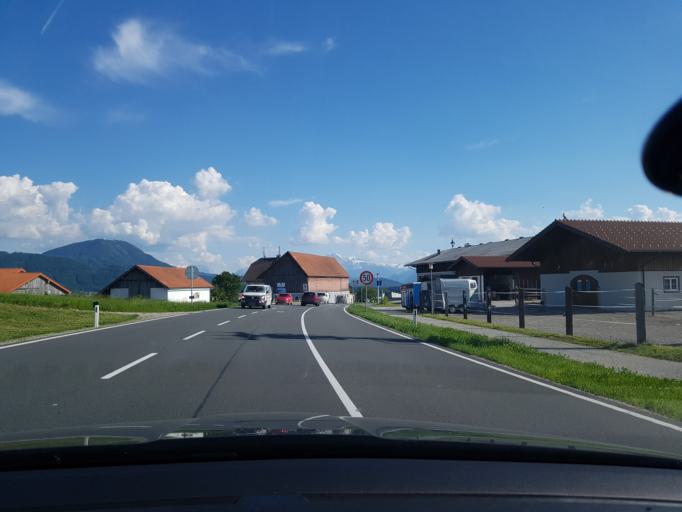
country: AT
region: Salzburg
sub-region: Politischer Bezirk Salzburg-Umgebung
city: Elixhausen
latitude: 47.8765
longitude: 13.0664
